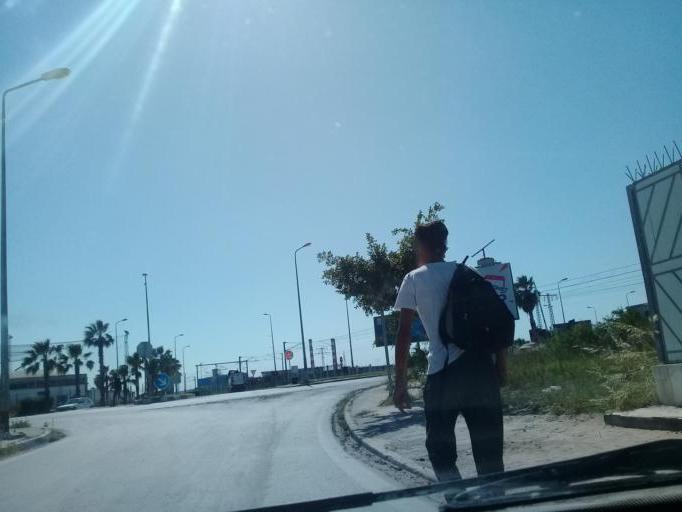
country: TN
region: Tunis
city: La Goulette
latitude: 36.8163
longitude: 10.2992
